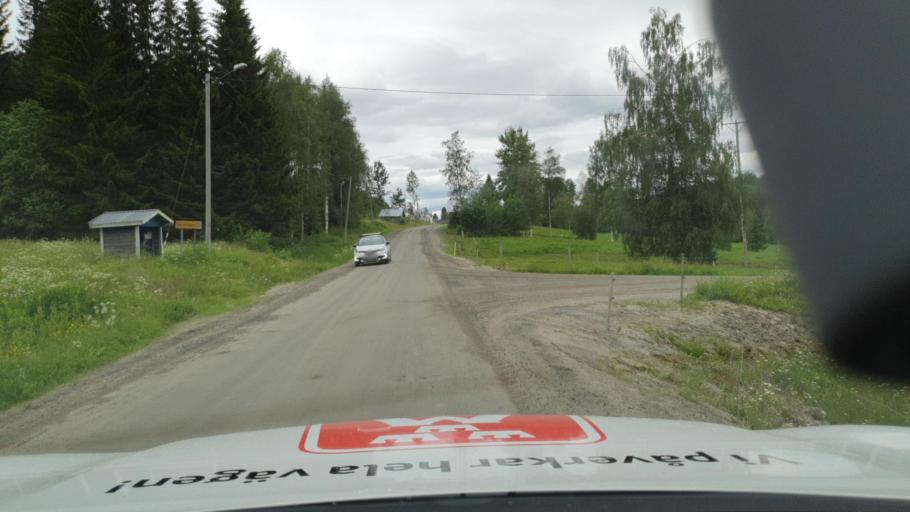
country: SE
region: Vaesterbotten
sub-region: Nordmalings Kommun
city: Nordmaling
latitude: 63.6642
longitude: 19.4413
